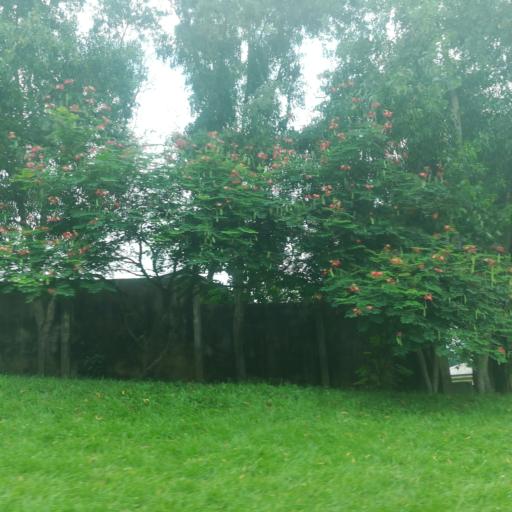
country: NG
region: Lagos
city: Ejirin
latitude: 6.6425
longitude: 3.7239
